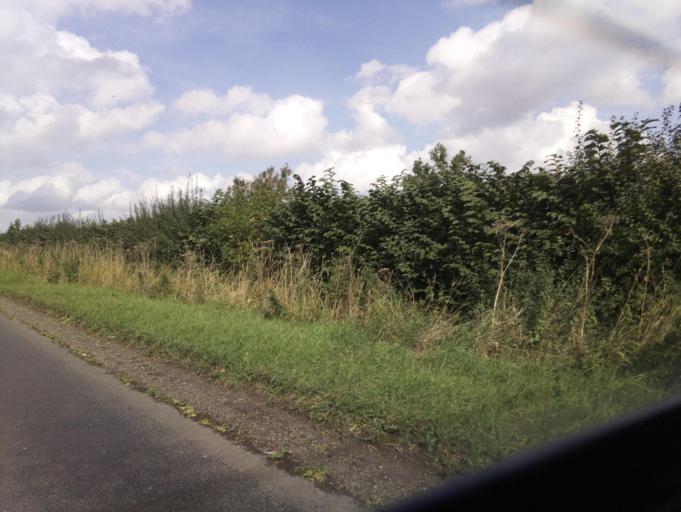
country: GB
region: England
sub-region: Darlington
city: High Coniscliffe
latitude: 54.5023
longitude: -1.6709
